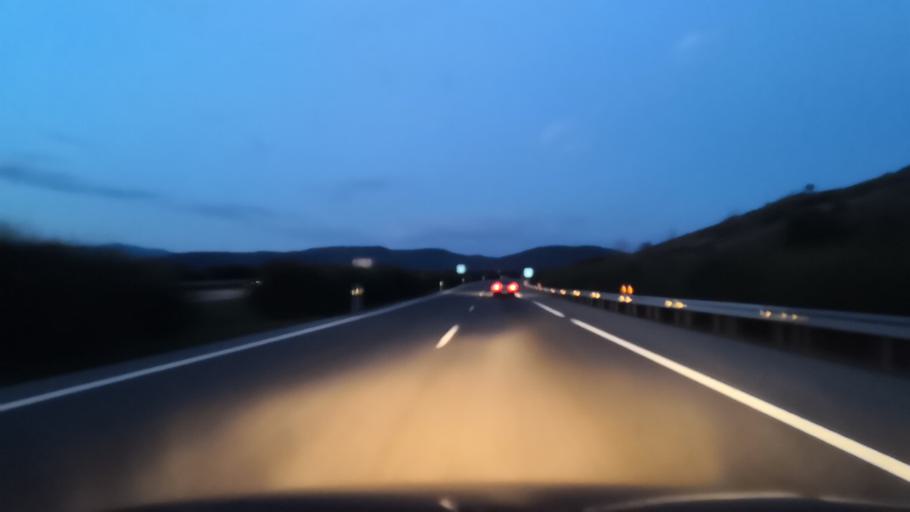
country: ES
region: Castille and Leon
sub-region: Provincia de Leon
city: Torre del Bierzo
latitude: 42.6097
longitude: -6.3446
